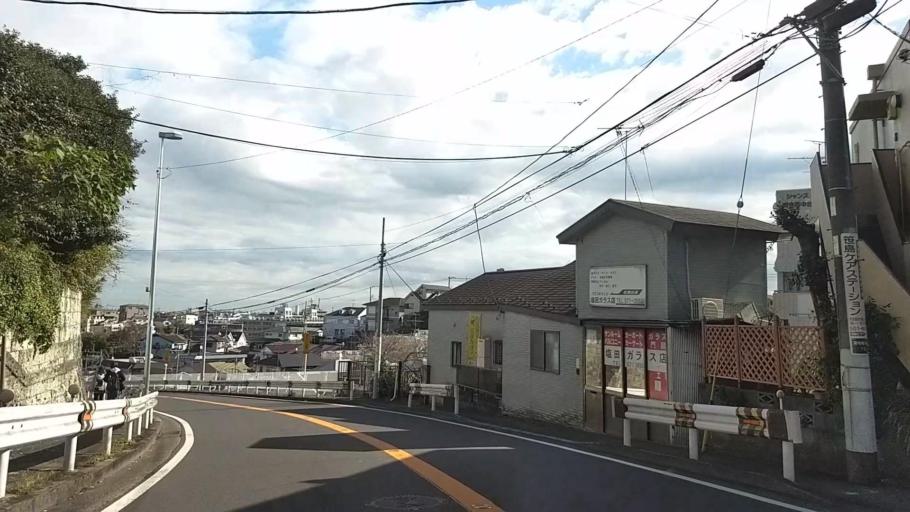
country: JP
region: Kanagawa
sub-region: Kawasaki-shi
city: Kawasaki
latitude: 35.5096
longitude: 139.6650
